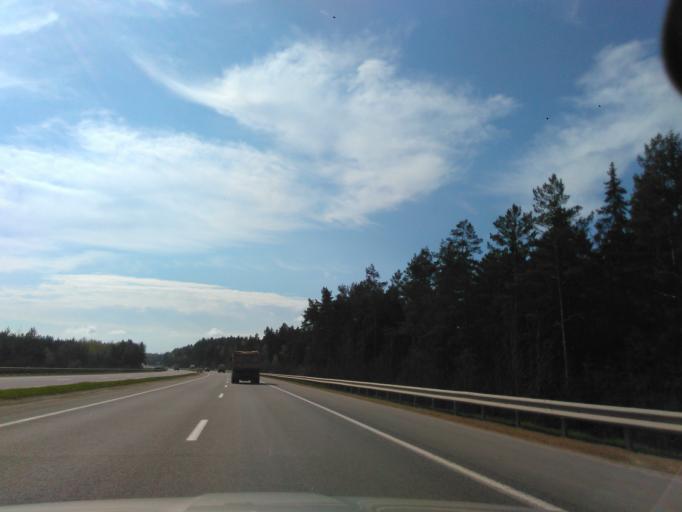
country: BY
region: Minsk
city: Rakaw
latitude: 53.9462
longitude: 27.1216
